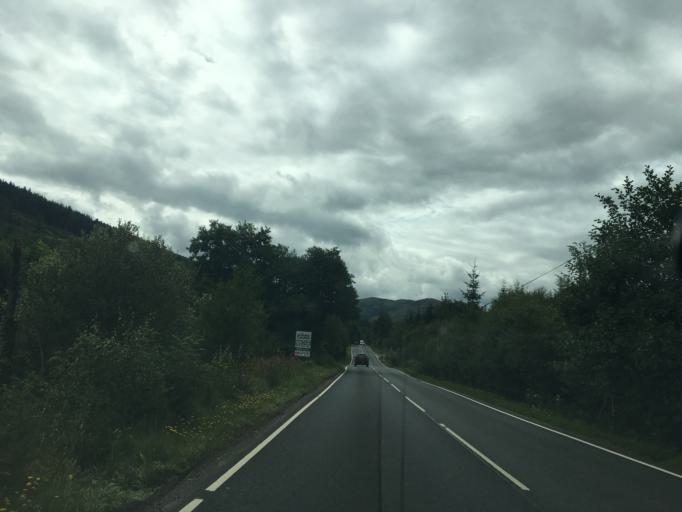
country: GB
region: Scotland
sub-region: Stirling
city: Callander
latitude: 56.3646
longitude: -4.3018
